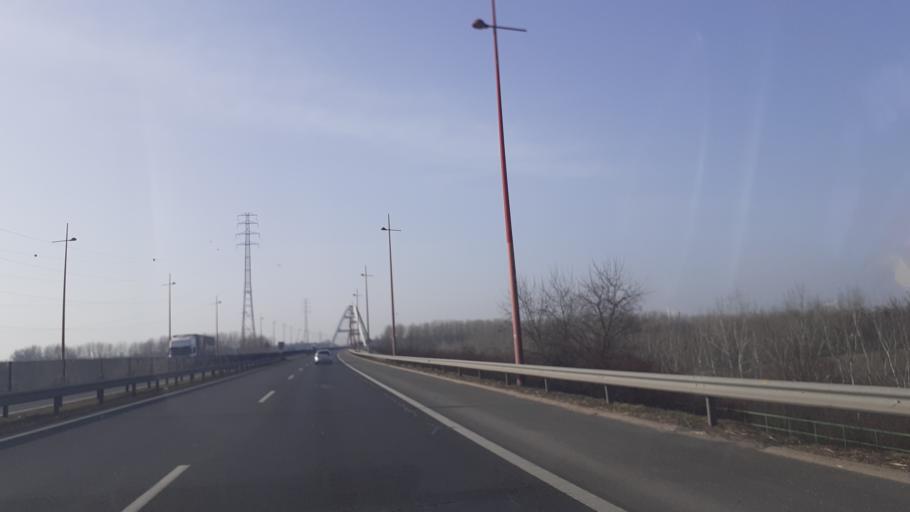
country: HU
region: Bacs-Kiskun
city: Dunavecse
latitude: 46.9001
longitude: 18.9684
